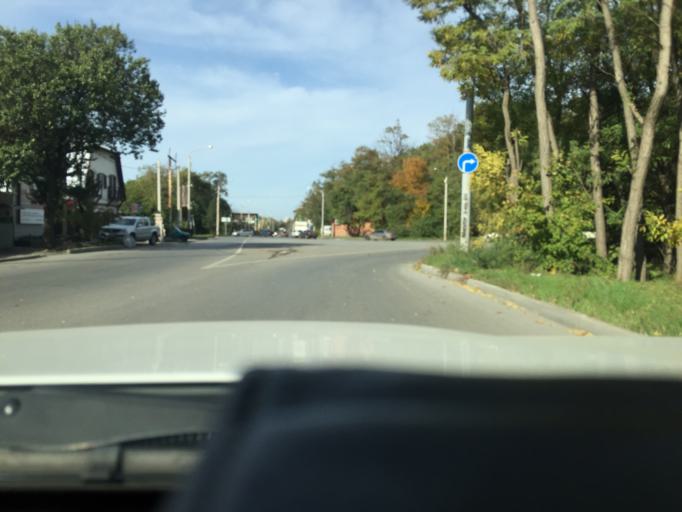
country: RU
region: Rostov
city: Imeni Chkalova
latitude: 47.2742
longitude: 39.7957
